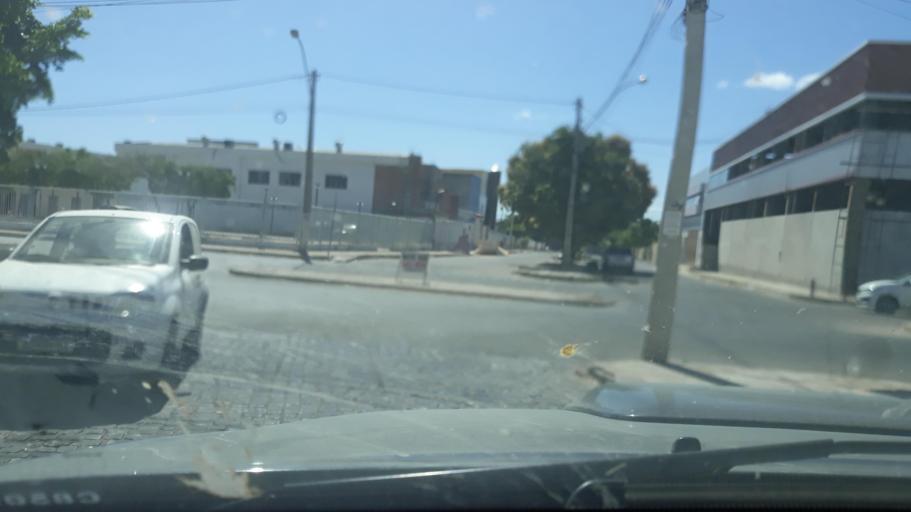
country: BR
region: Bahia
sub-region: Guanambi
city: Guanambi
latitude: -14.2192
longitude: -42.7844
